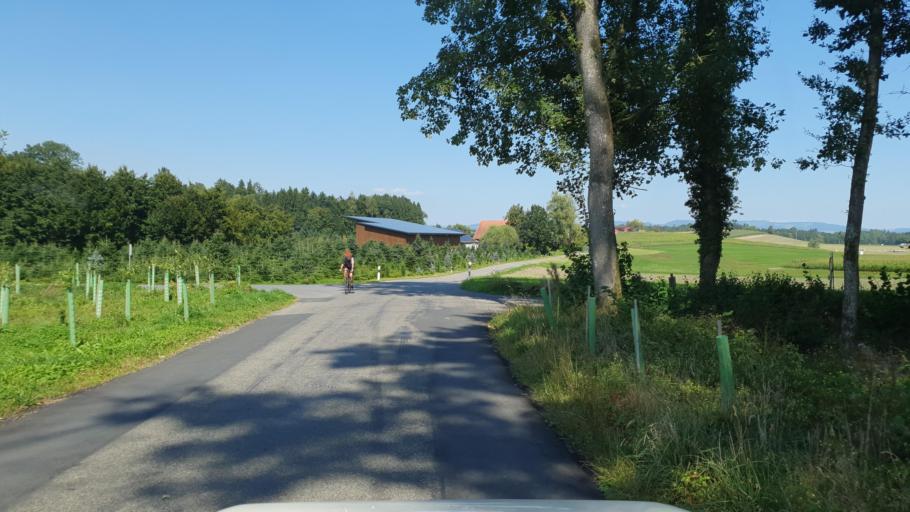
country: CH
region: Lucerne
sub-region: Hochdorf District
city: Inwil
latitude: 47.1540
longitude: 8.3622
